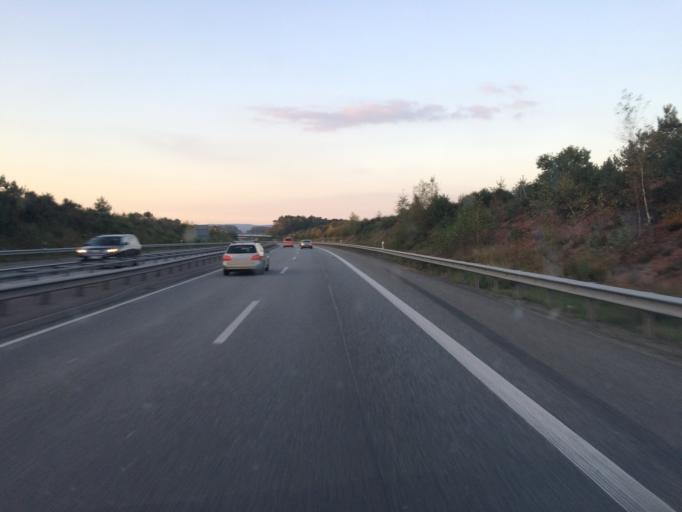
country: DE
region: Rheinland-Pfalz
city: Mehlingen
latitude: 49.4878
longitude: 7.8415
